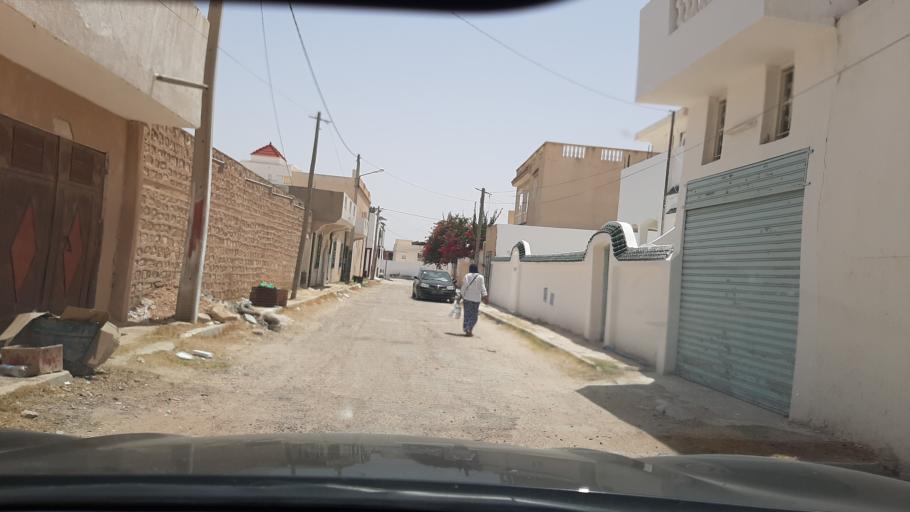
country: TN
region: Qabis
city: Matmata
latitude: 33.6185
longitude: 10.2828
